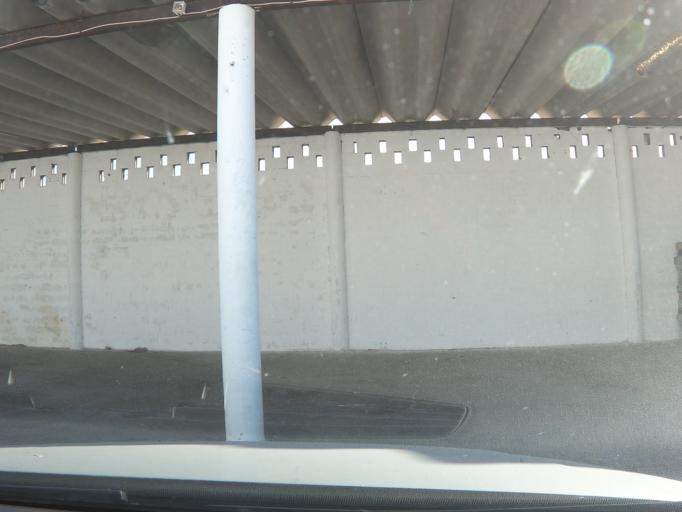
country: PT
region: Setubal
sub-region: Setubal
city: Setubal
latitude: 38.4865
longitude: -8.8864
